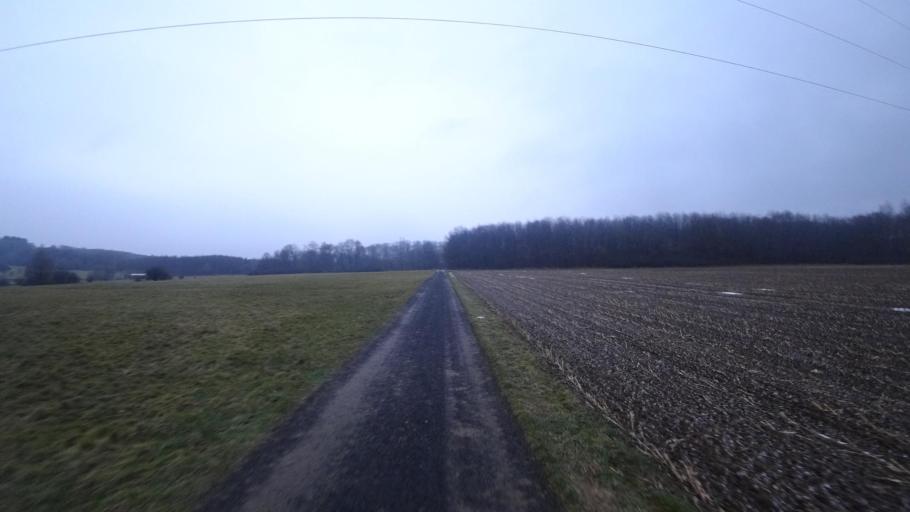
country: DE
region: Rheinland-Pfalz
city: Ailertchen
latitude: 50.6057
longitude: 7.9206
